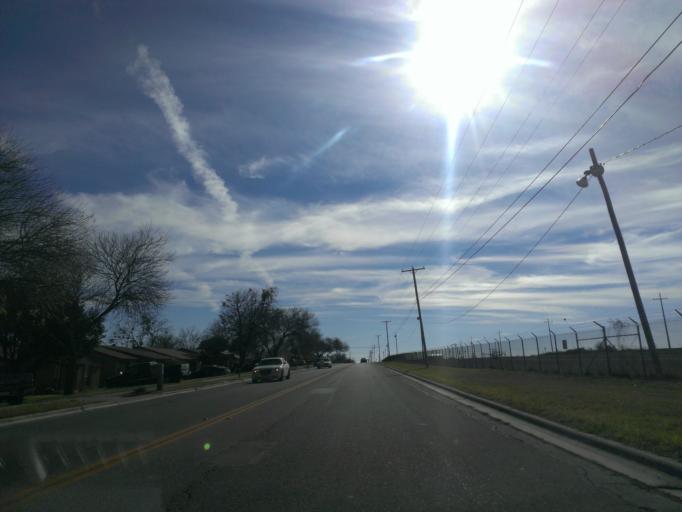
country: US
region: Texas
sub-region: Bell County
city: Killeen
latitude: 31.1378
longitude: -97.7038
